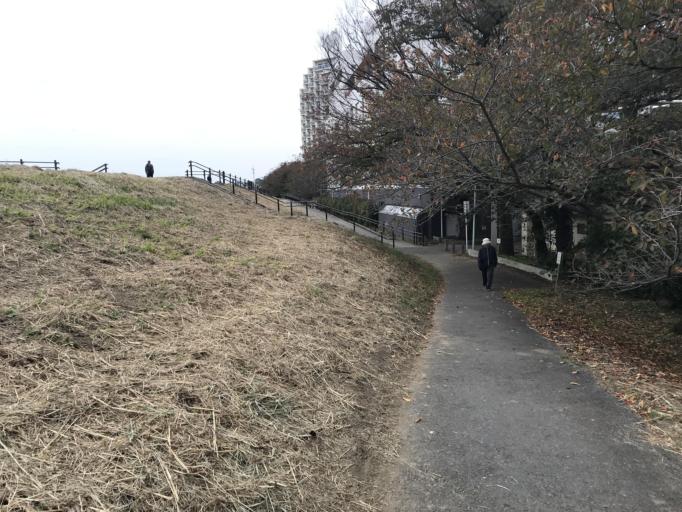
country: JP
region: Kanagawa
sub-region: Kawasaki-shi
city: Kawasaki
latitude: 35.5733
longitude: 139.6759
